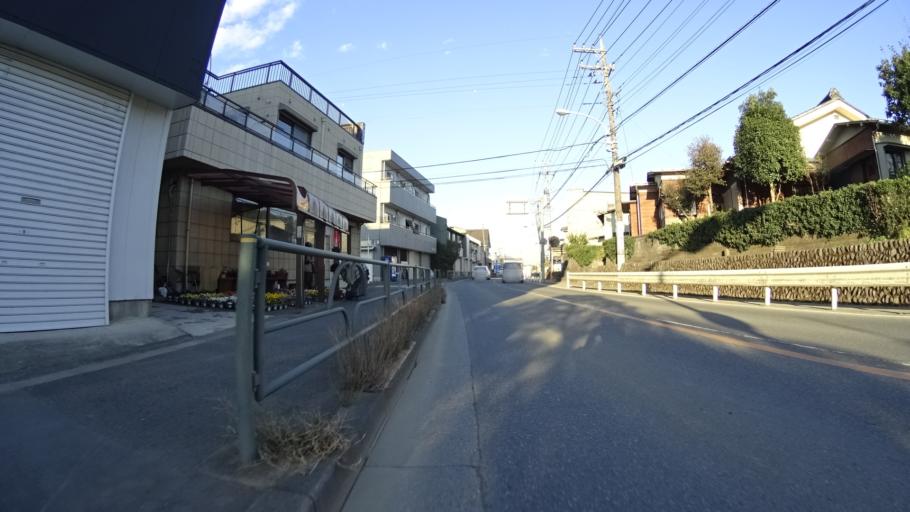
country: JP
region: Tokyo
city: Hachioji
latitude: 35.6791
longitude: 139.2715
